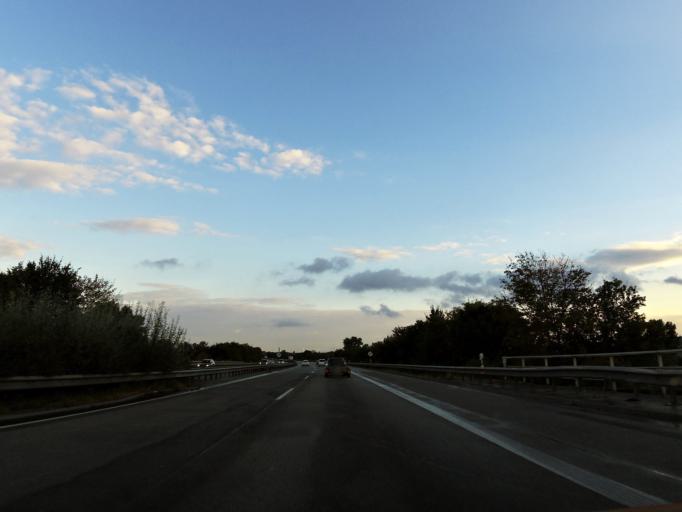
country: DE
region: Rheinland-Pfalz
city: Gensingen
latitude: 49.8873
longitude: 7.9457
